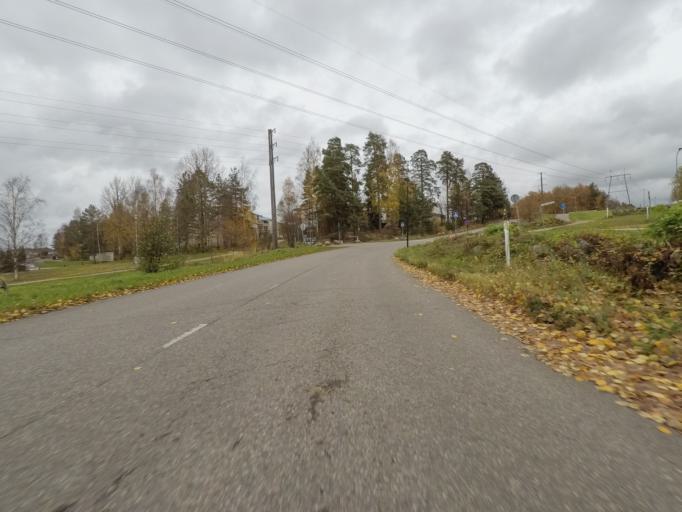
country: FI
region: Uusimaa
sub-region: Porvoo
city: Porvoo
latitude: 60.4072
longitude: 25.6664
